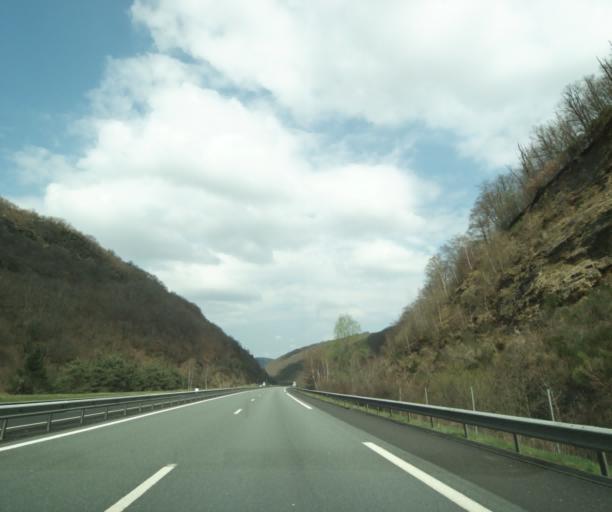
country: FR
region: Auvergne
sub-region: Departement du Cantal
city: Massiac
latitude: 45.2039
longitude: 3.1965
